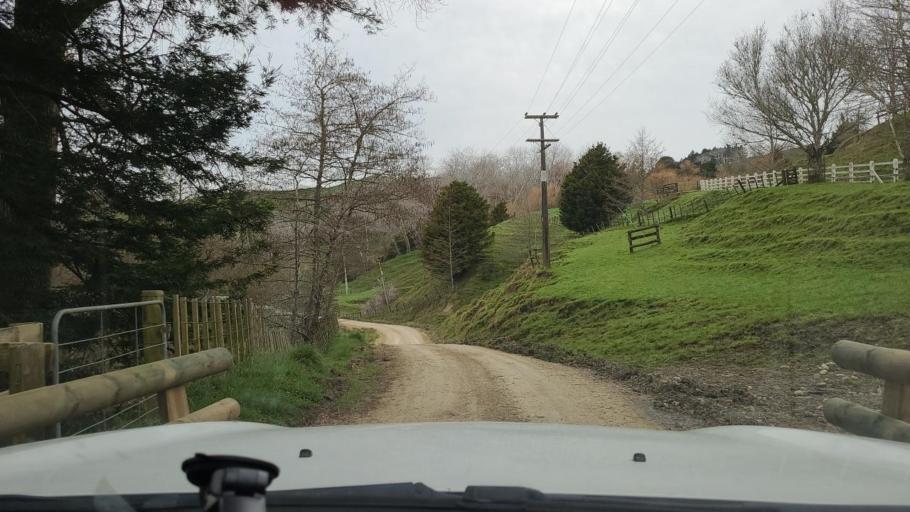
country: NZ
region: Gisborne
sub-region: Gisborne District
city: Gisborne
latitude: -38.4970
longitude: 178.0851
